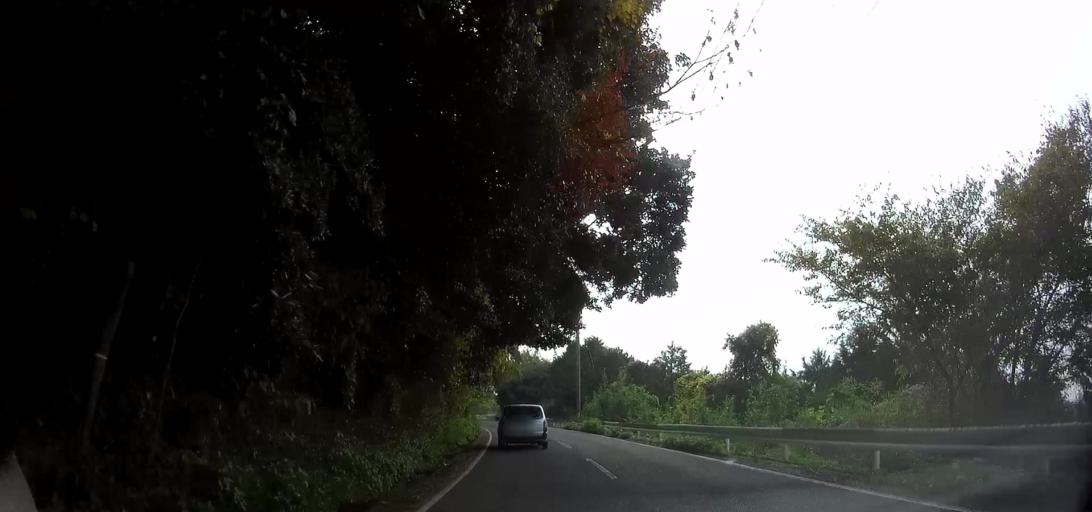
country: JP
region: Nagasaki
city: Shimabara
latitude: 32.6863
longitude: 130.2774
